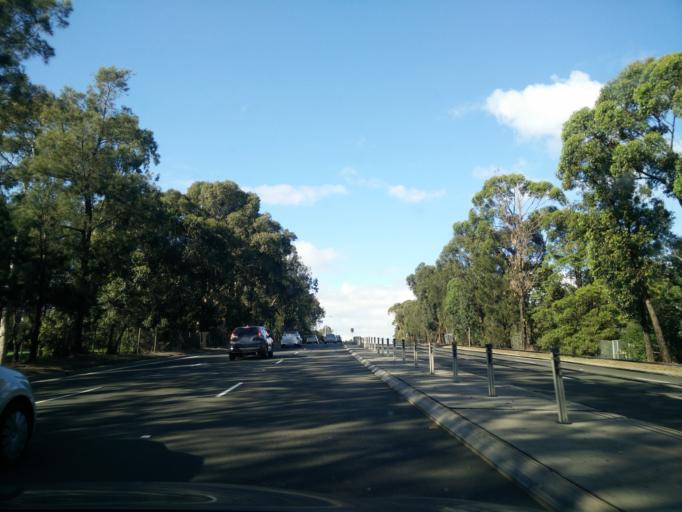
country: AU
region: New South Wales
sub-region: Strathfield
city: Homebush
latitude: -33.8733
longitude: 151.0664
